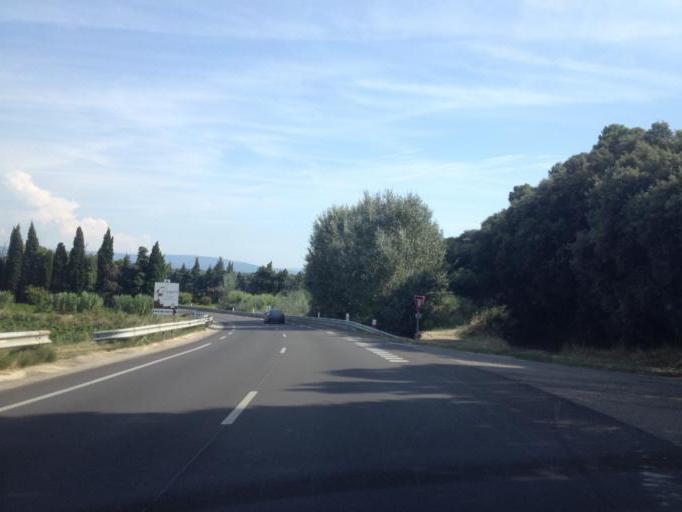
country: FR
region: Provence-Alpes-Cote d'Azur
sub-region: Departement du Vaucluse
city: Vacqueyras
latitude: 44.1257
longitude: 4.9984
